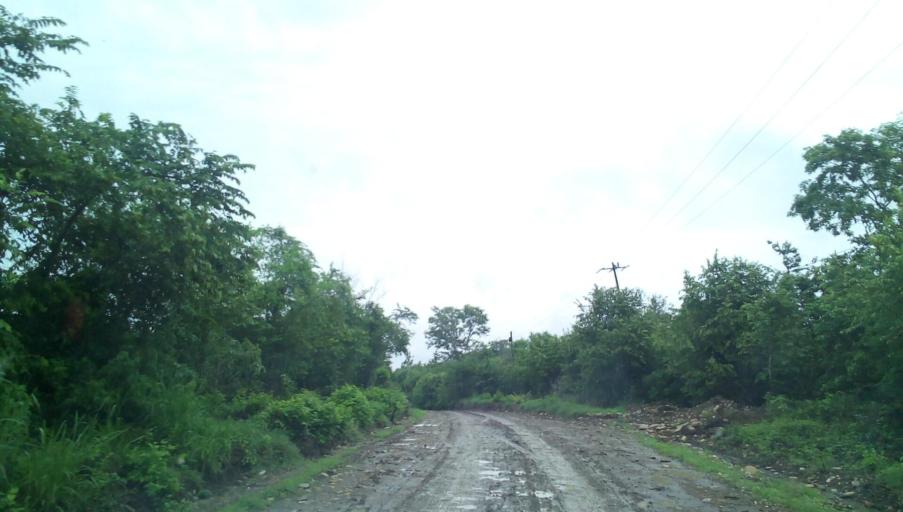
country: MX
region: Veracruz
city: Tempoal de Sanchez
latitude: 21.4408
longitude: -98.4226
